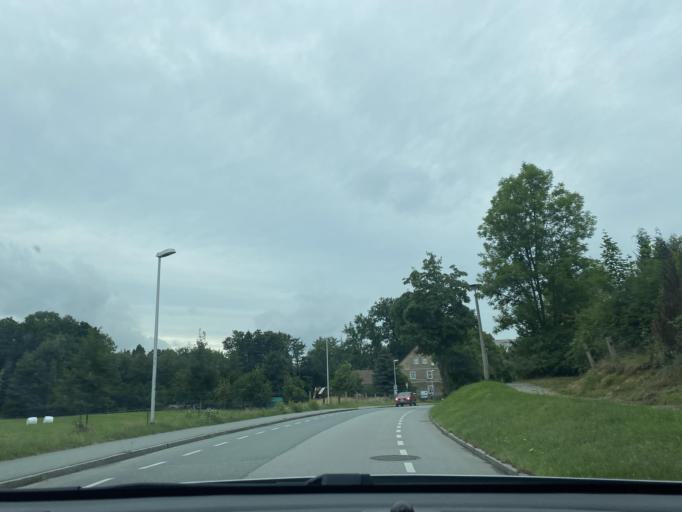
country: DE
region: Saxony
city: Lobau
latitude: 51.0899
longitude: 14.6749
